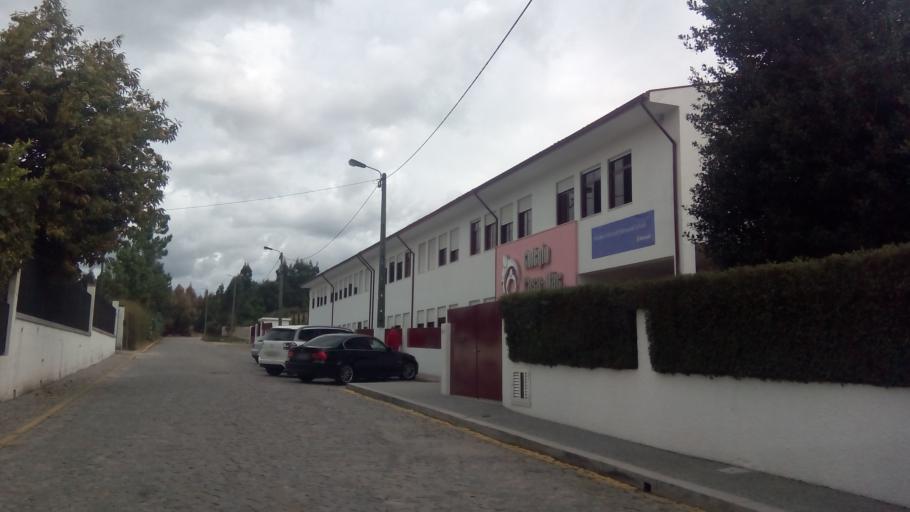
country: PT
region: Porto
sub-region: Paredes
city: Baltar
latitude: 41.1865
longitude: -8.3712
